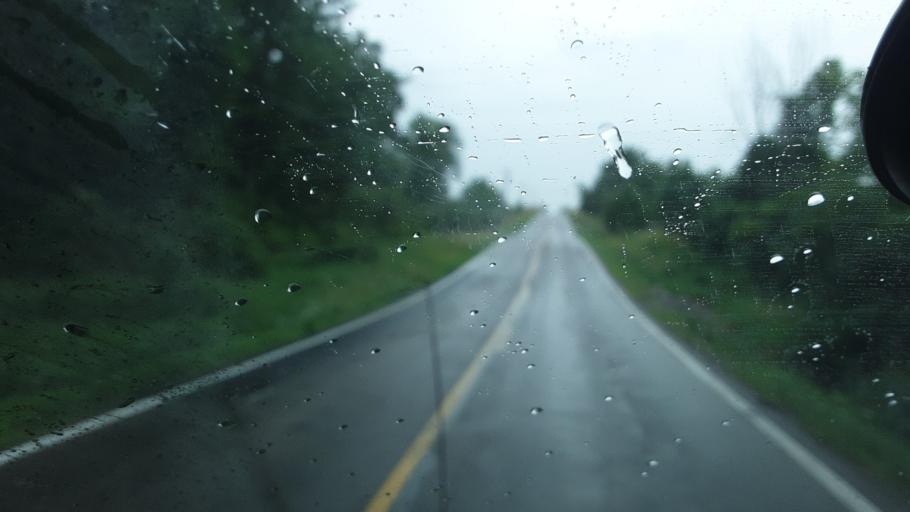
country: US
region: Ohio
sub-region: Williams County
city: Montpelier
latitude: 41.5210
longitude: -84.6129
